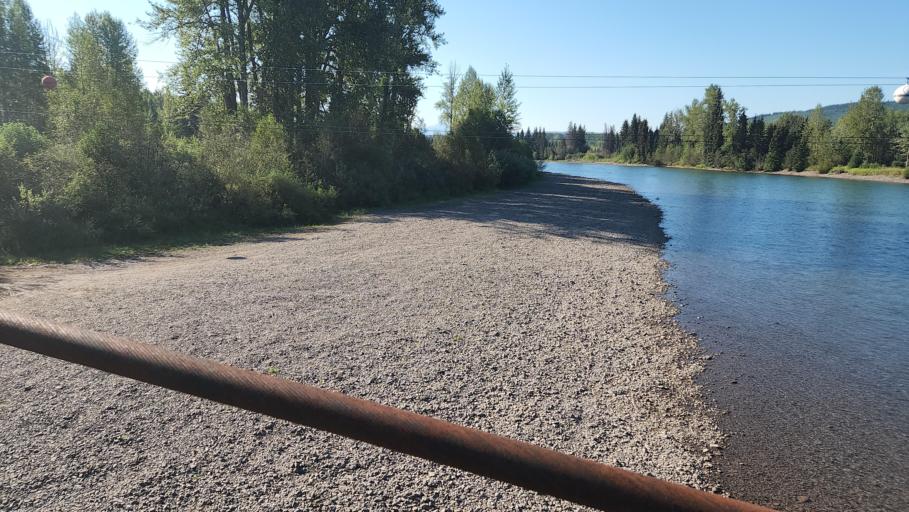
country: CA
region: British Columbia
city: Houston
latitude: 54.5175
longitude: -126.8389
